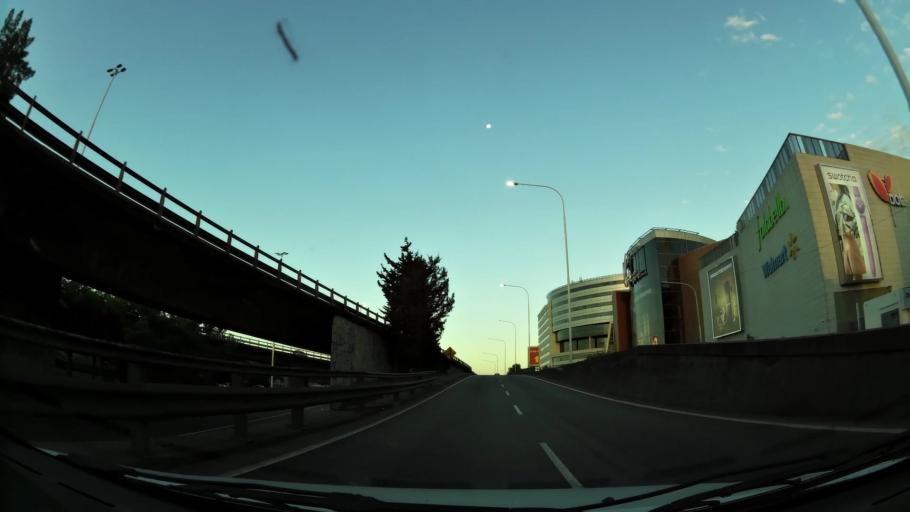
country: AR
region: Buenos Aires
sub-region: Partido de Vicente Lopez
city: Olivos
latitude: -34.5459
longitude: -58.4897
